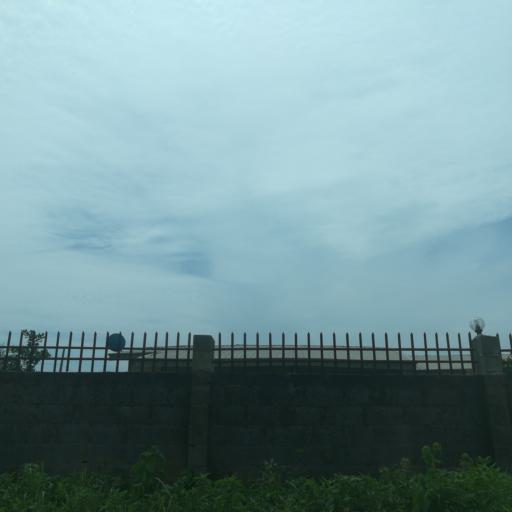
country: NG
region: Lagos
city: Ejirin
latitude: 6.6358
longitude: 3.7101
